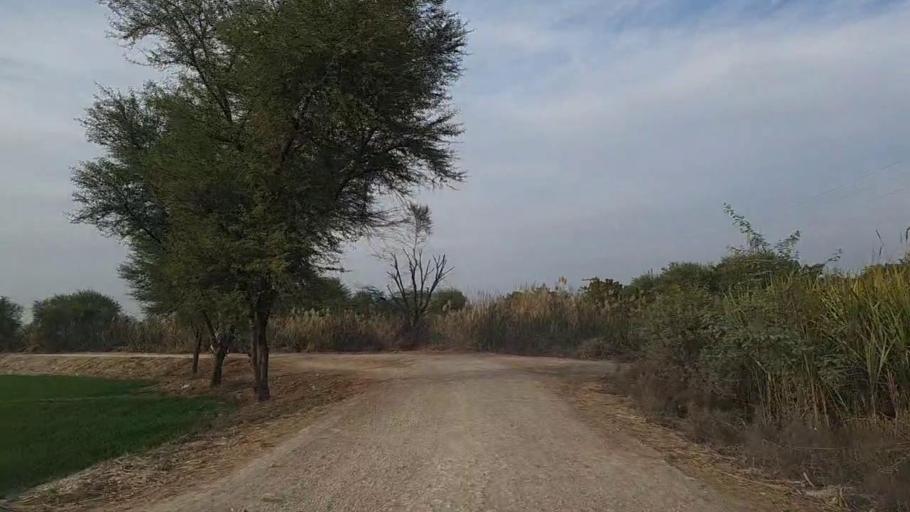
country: PK
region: Sindh
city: Daur
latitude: 26.5255
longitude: 68.4073
